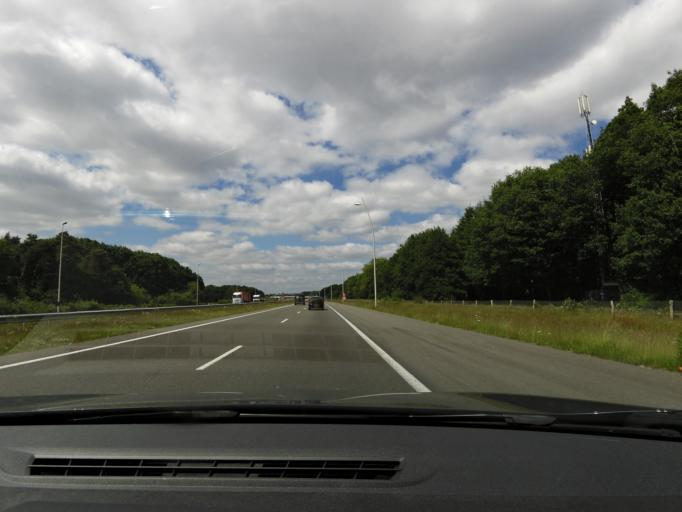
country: NL
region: North Brabant
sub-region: Gemeente Loon op Zand
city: Loon op Zand
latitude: 51.6149
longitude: 5.0700
